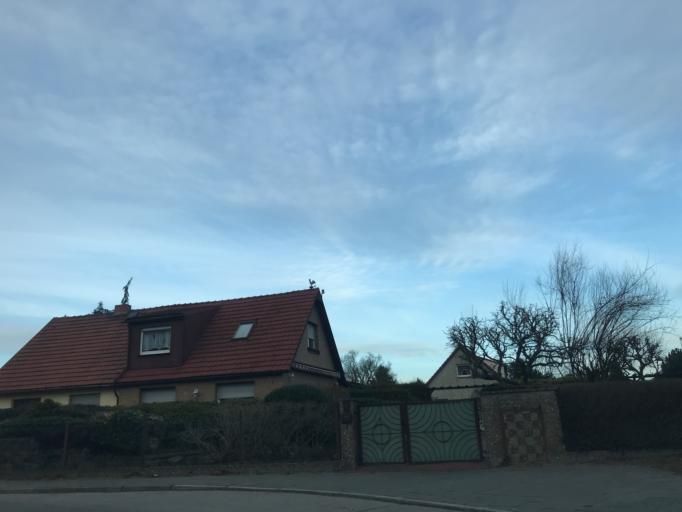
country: DE
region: Berlin
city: Falkenhagener Feld
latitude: 52.5565
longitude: 13.1499
